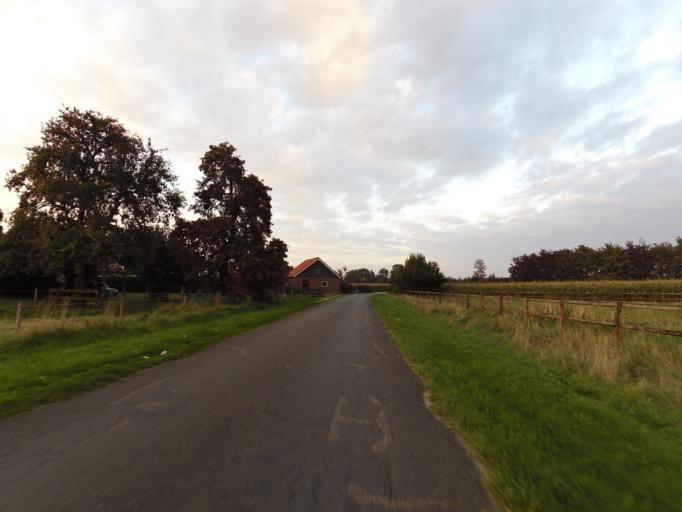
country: NL
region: Gelderland
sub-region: Gemeente Doetinchem
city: Doetinchem
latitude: 51.9469
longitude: 6.2470
